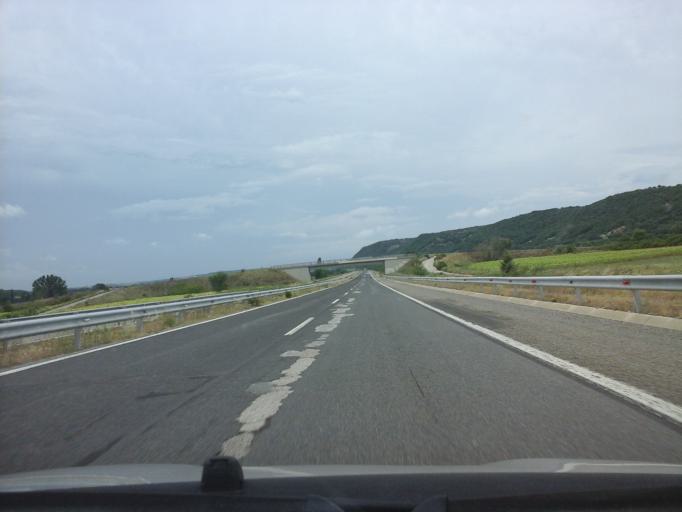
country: GR
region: East Macedonia and Thrace
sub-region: Nomos Evrou
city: Feres
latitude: 40.9298
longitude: 26.1652
